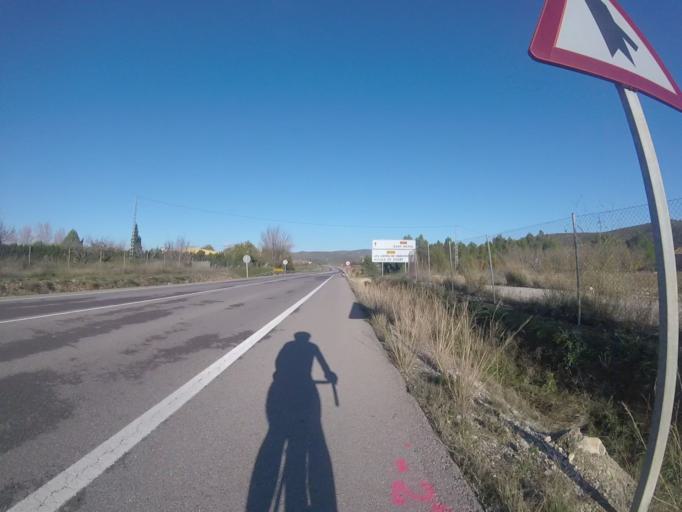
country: ES
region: Valencia
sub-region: Provincia de Castello
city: Cuevas de Vinroma
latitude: 40.3155
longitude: 0.1210
